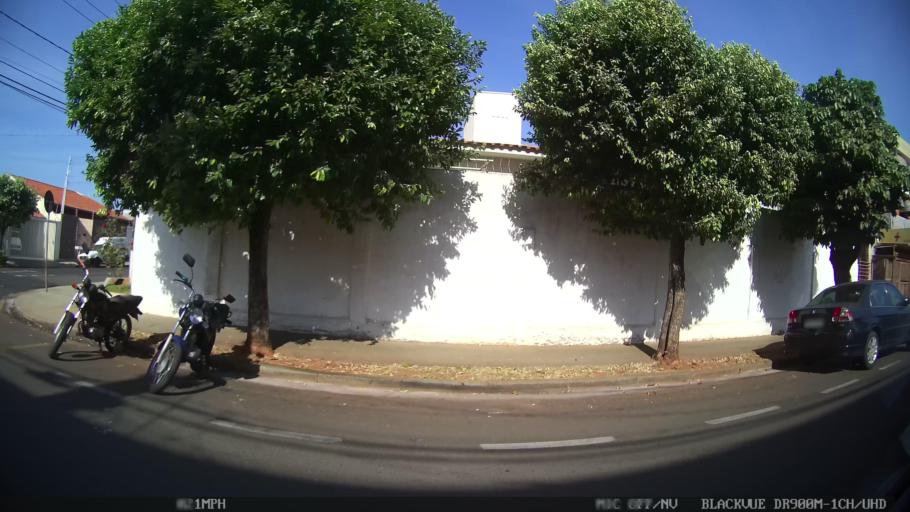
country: BR
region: Sao Paulo
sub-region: Sao Jose Do Rio Preto
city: Sao Jose do Rio Preto
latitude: -20.8054
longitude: -49.3947
